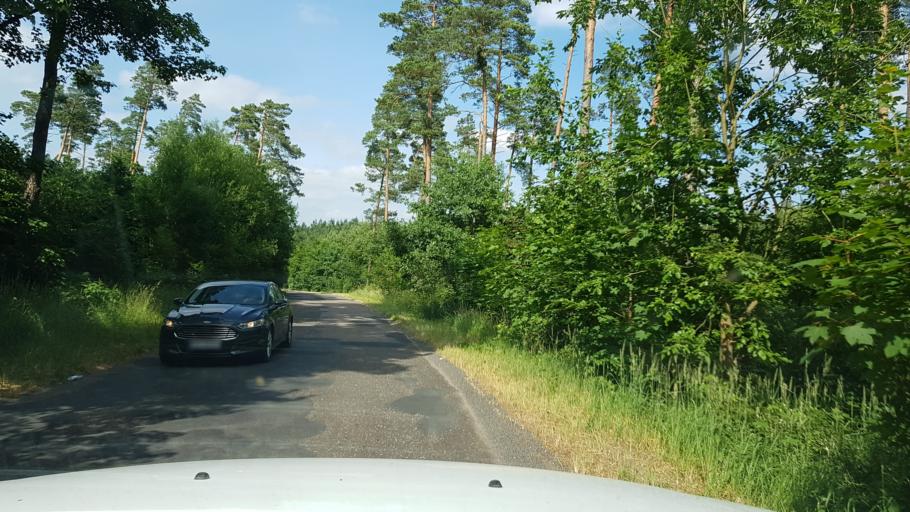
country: PL
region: West Pomeranian Voivodeship
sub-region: Powiat goleniowski
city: Mosty
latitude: 53.5518
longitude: 14.9638
